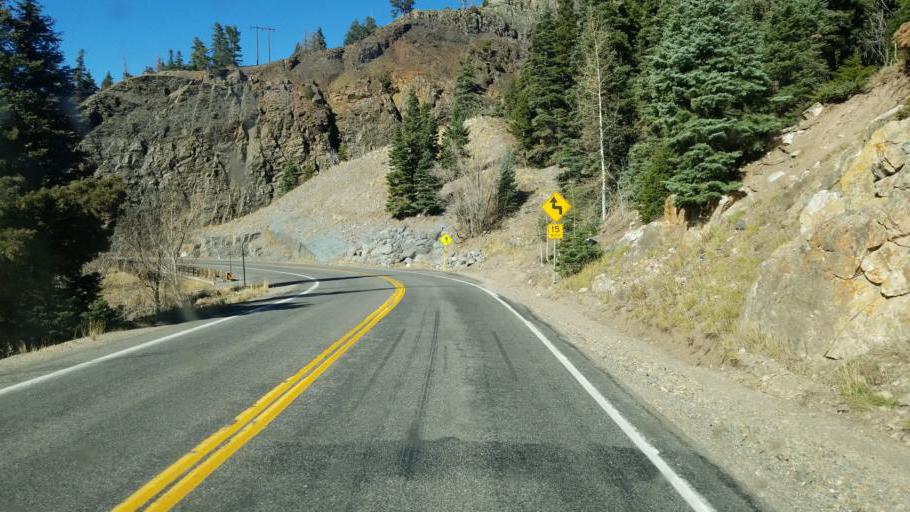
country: US
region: Colorado
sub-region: Ouray County
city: Ouray
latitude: 37.9990
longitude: -107.6592
